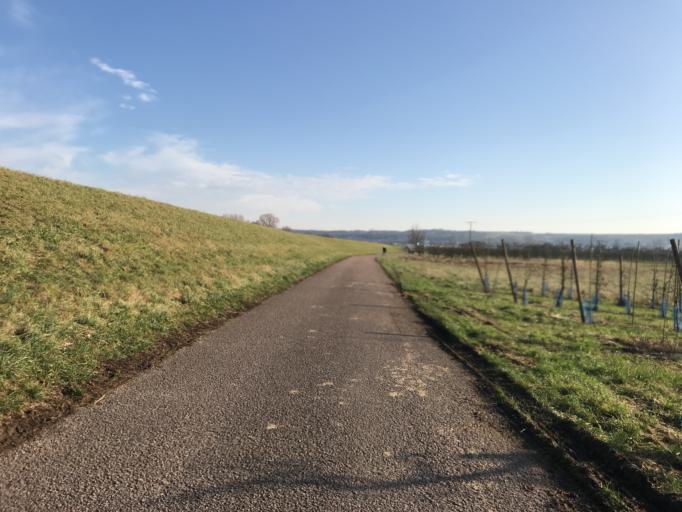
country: DE
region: Hesse
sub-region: Regierungsbezirk Darmstadt
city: Eltville
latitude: 50.0111
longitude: 8.1065
